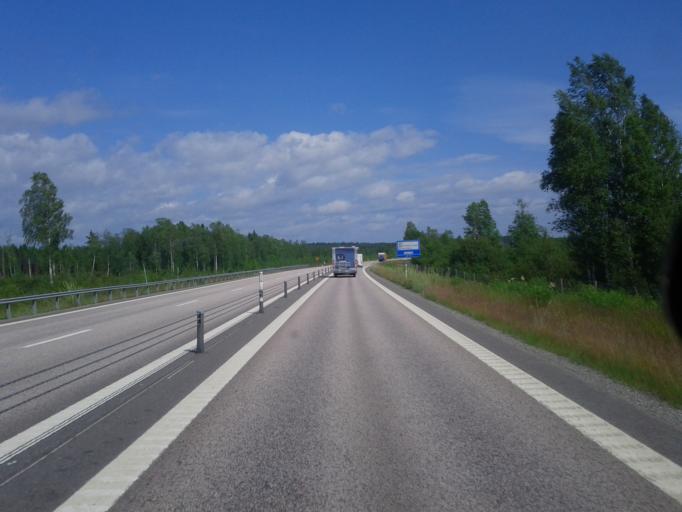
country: SE
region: Vaesterbotten
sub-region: Nordmalings Kommun
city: Nordmaling
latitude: 63.5692
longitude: 19.4359
